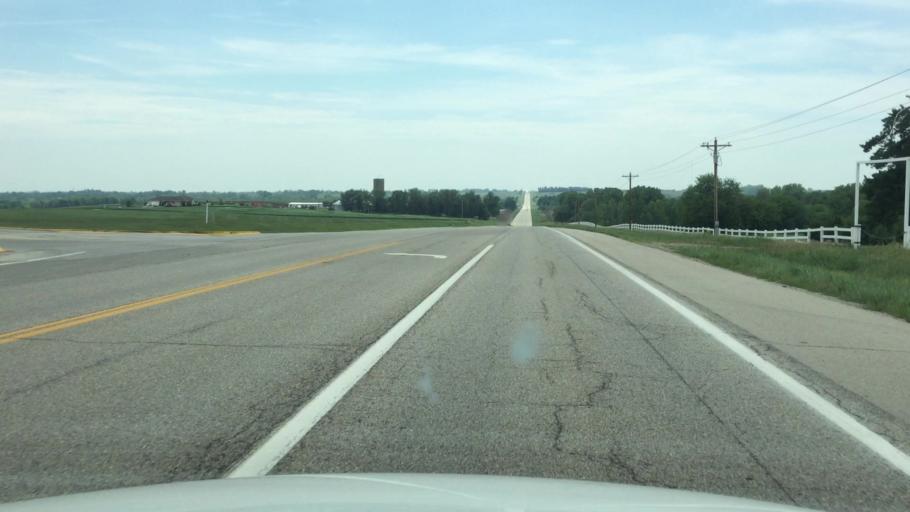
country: US
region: Kansas
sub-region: Brown County
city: Horton
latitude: 39.7000
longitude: -95.7303
